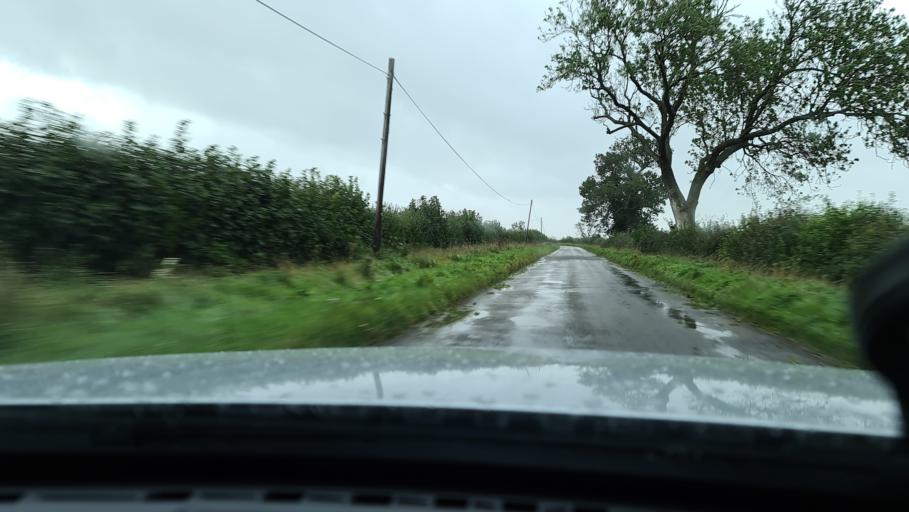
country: GB
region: England
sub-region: Oxfordshire
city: Woodstock
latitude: 51.9171
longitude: -1.3694
